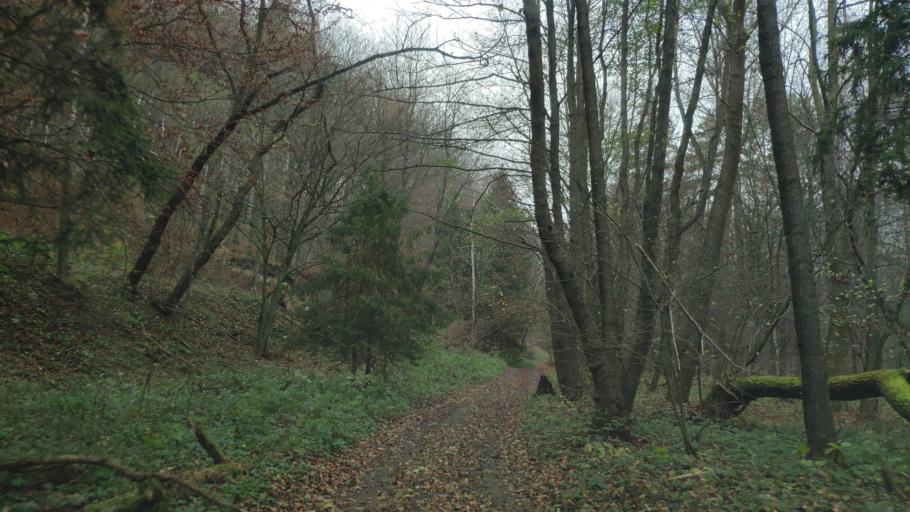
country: SK
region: Presovsky
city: Sabinov
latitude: 49.1447
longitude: 21.2135
